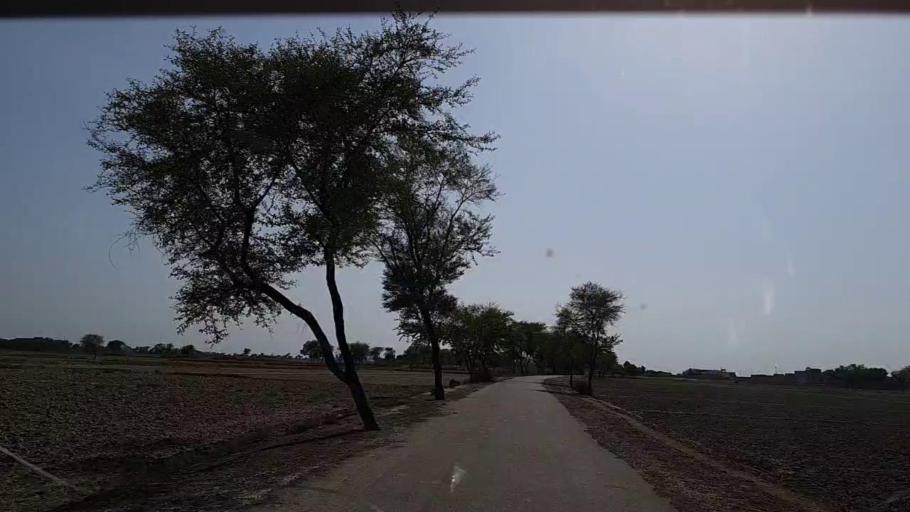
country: PK
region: Sindh
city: Phulji
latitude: 26.9219
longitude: 67.6783
